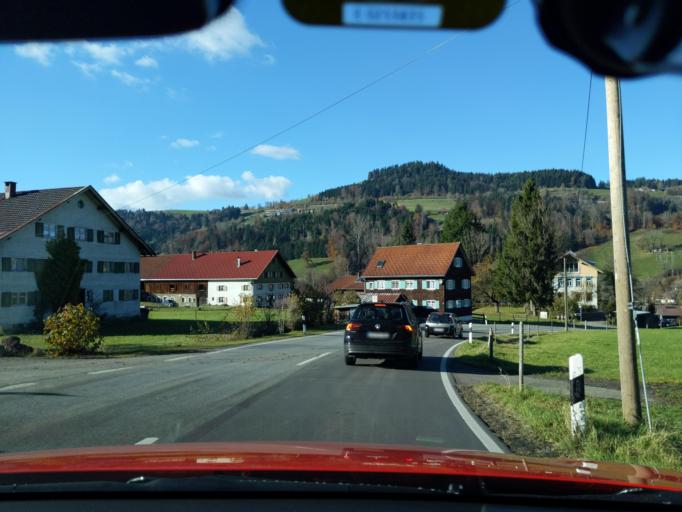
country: DE
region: Bavaria
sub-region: Swabia
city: Oberstaufen
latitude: 47.5389
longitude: 10.0177
